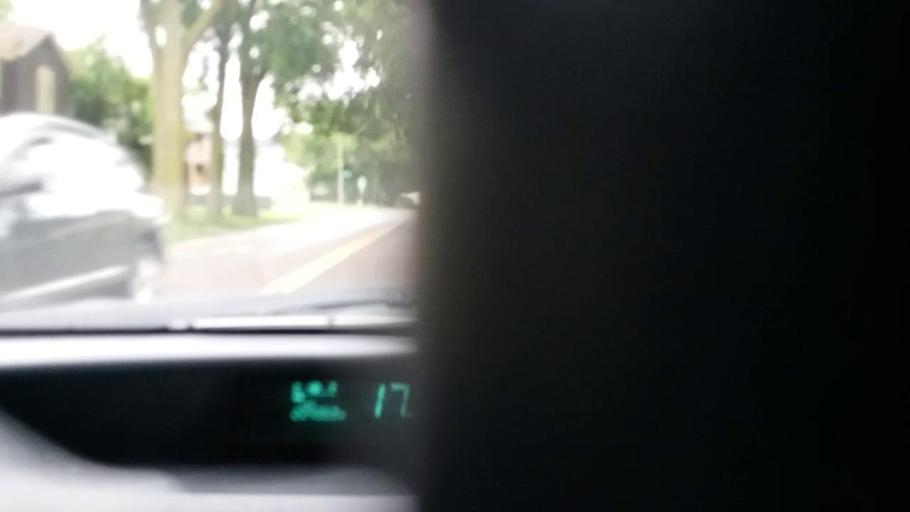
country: US
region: Illinois
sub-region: Peoria County
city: Peoria
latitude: 40.7035
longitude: -89.6036
